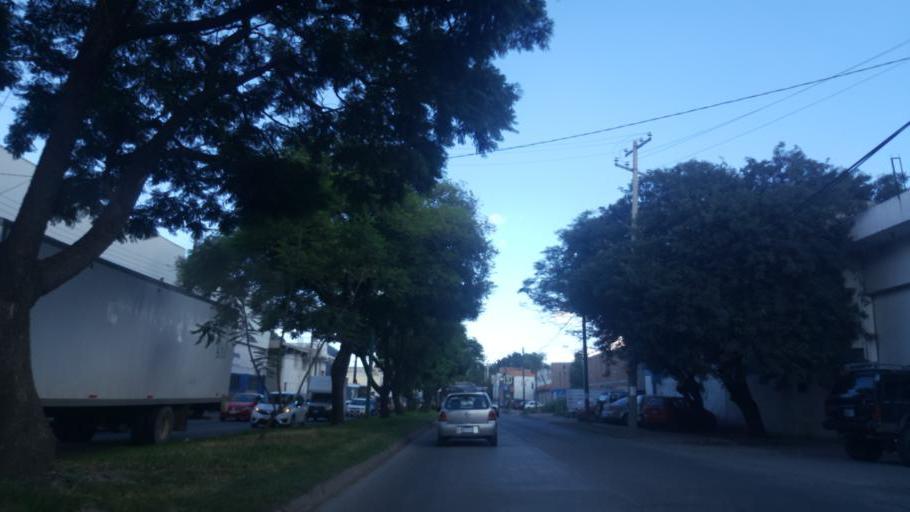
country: MX
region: Guanajuato
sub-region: Leon
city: San Jose de Duran (Los Troncoso)
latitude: 21.0929
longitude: -101.6859
